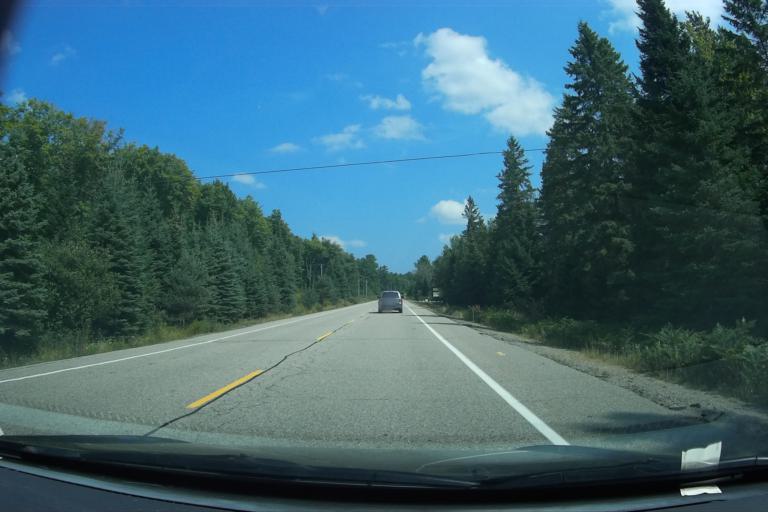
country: CA
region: Ontario
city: Mattawa
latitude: 45.5846
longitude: -78.4887
